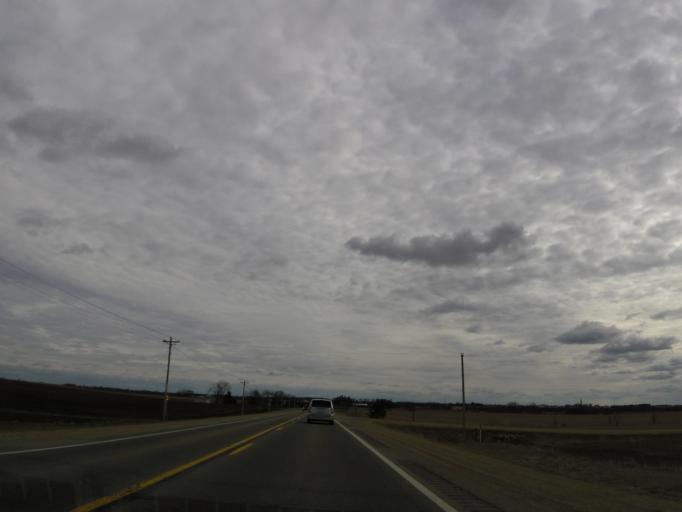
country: US
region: Iowa
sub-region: Chickasaw County
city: New Hampton
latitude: 43.1062
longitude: -92.2979
